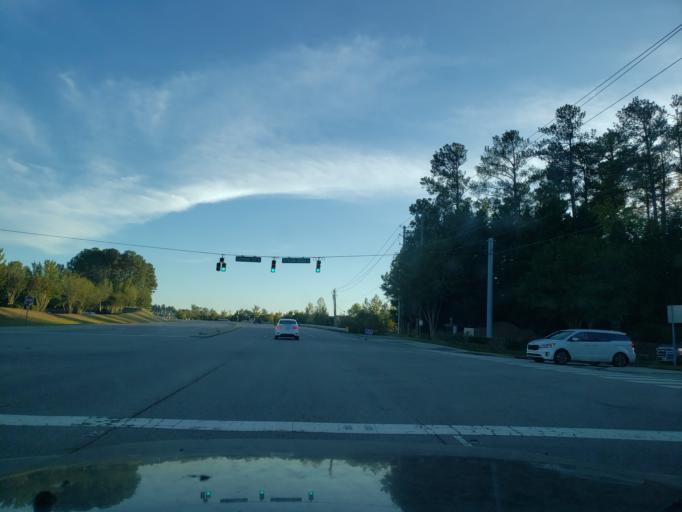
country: US
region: North Carolina
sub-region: Wake County
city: Morrisville
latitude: 35.8398
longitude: -78.8556
